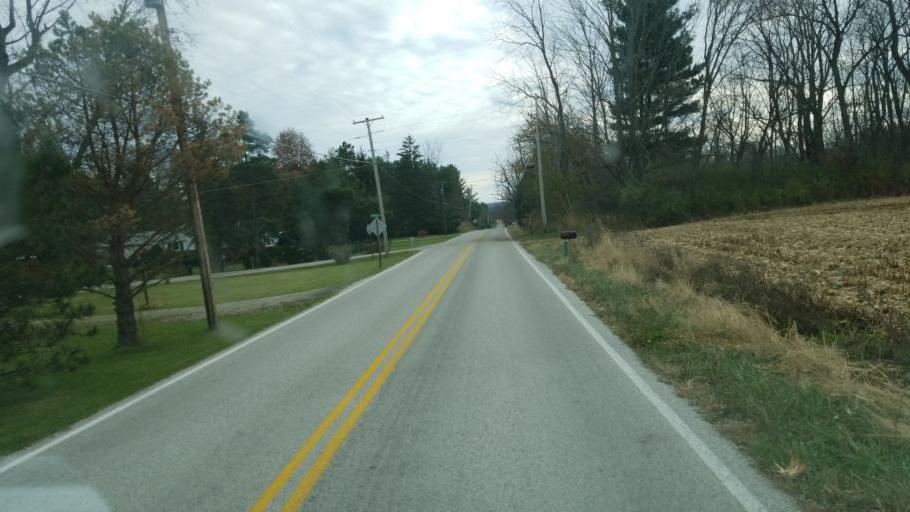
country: US
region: Ohio
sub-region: Crawford County
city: Crestline
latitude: 40.7357
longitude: -82.6712
